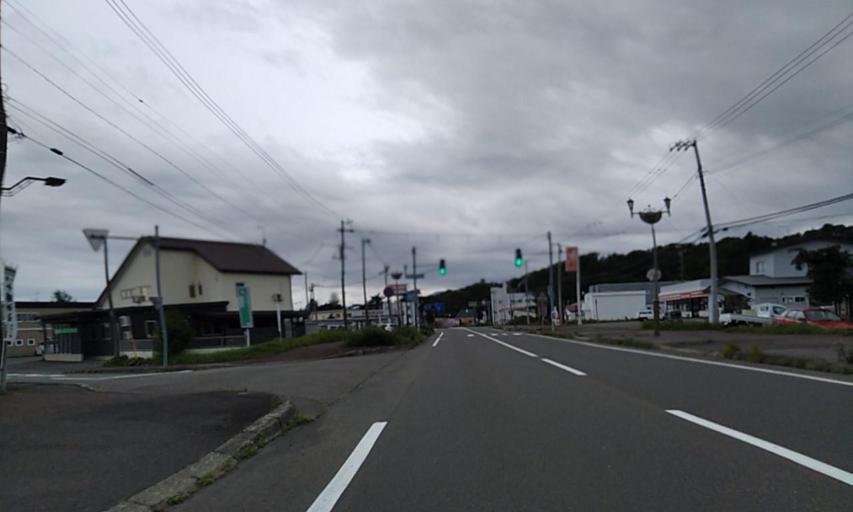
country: JP
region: Hokkaido
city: Obihiro
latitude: 42.2952
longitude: 143.3130
